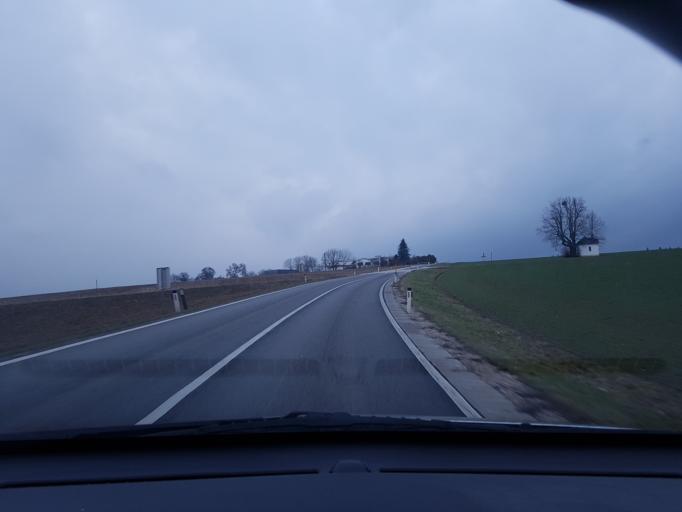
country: AT
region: Upper Austria
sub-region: Politischer Bezirk Steyr-Land
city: Sierning
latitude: 48.1188
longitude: 14.3482
